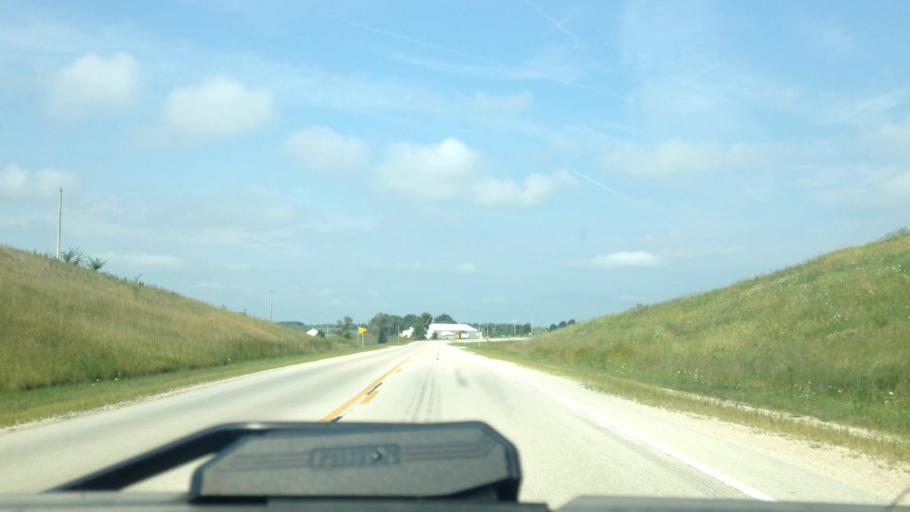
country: US
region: Wisconsin
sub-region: Dodge County
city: Theresa
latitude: 43.5367
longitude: -88.4403
